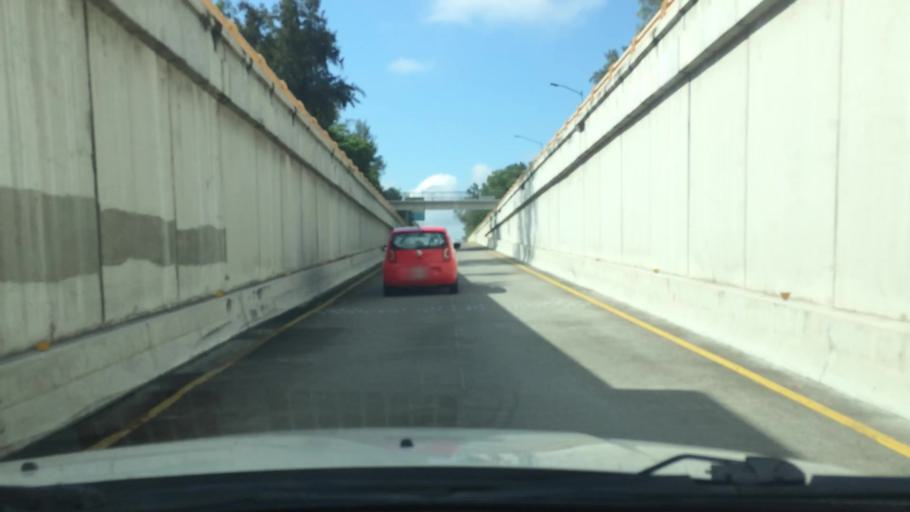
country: MX
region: Morelos
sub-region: Cuernavaca
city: Fraccionamiento Lomas de Ahuatlan
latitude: 18.9648
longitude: -99.2468
